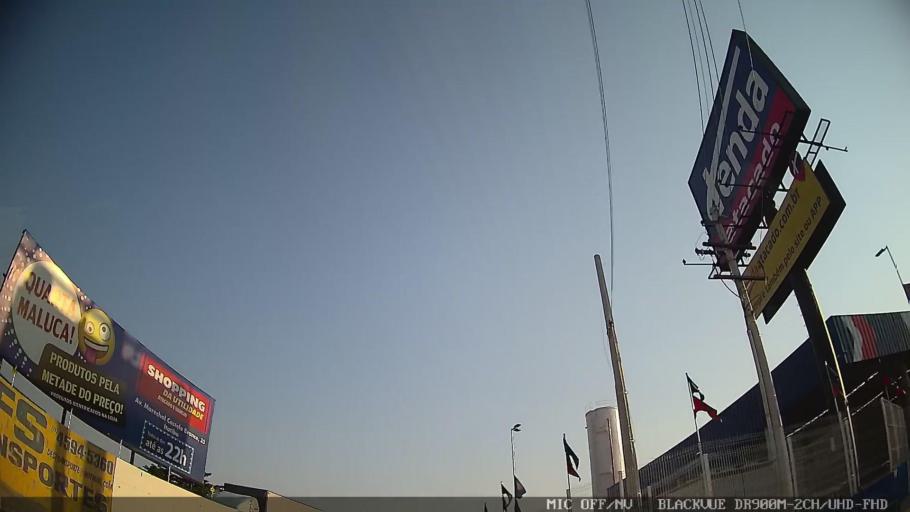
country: BR
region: Sao Paulo
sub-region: Itatiba
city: Itatiba
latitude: -23.0112
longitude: -46.8415
